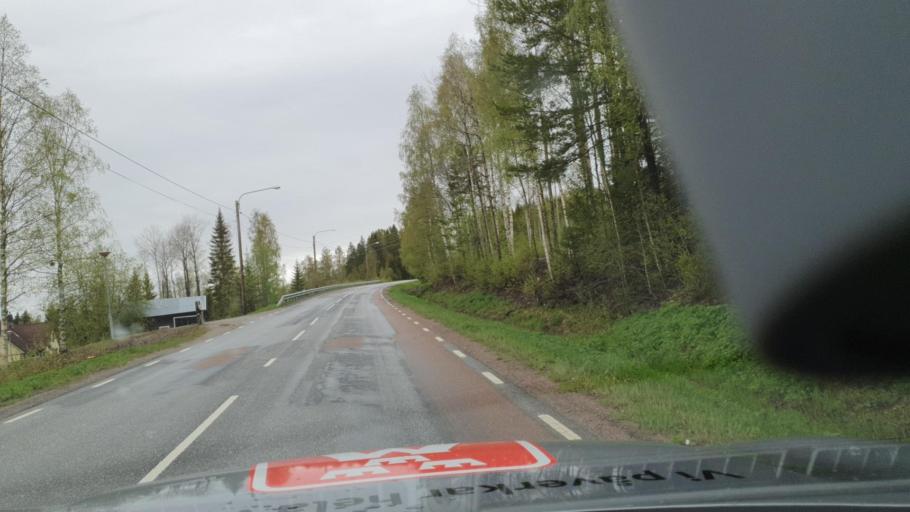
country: SE
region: Vaesternorrland
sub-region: OErnskoeldsviks Kommun
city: Bjasta
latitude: 63.3794
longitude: 18.4740
